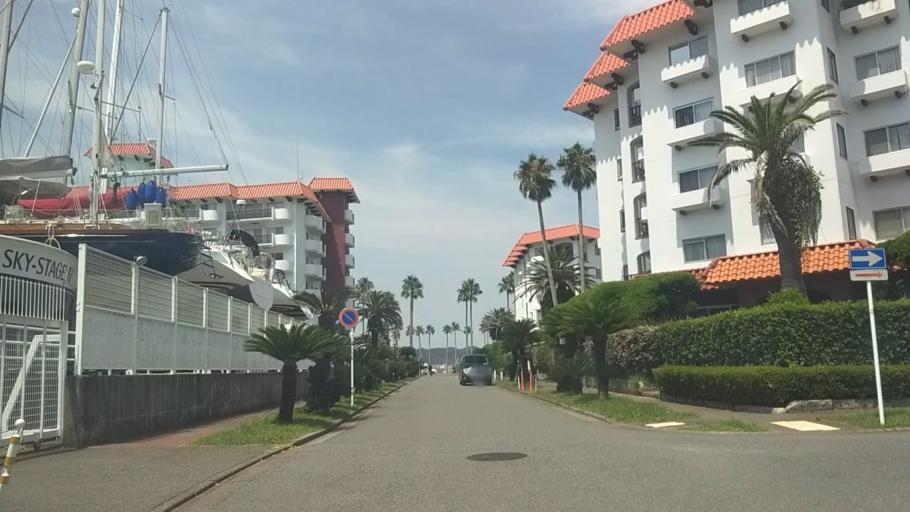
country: JP
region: Kanagawa
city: Kamakura
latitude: 35.2975
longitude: 139.5530
